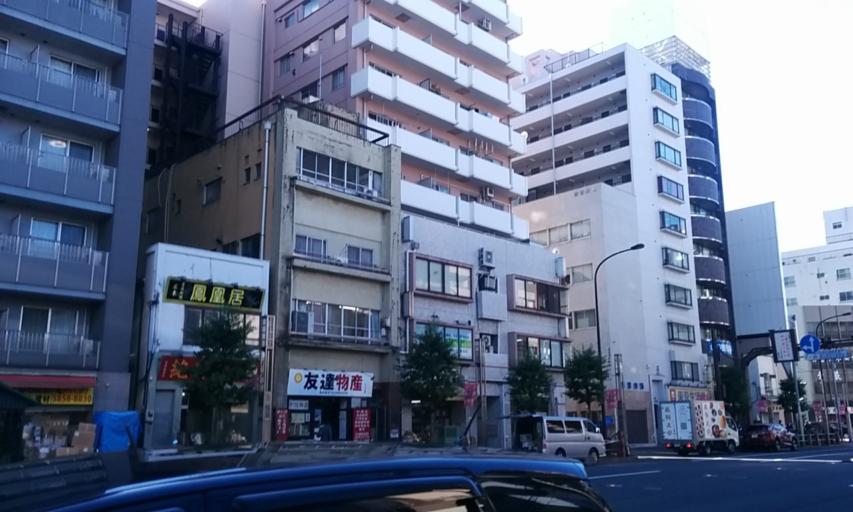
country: JP
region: Tokyo
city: Urayasu
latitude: 35.7018
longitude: 139.8242
